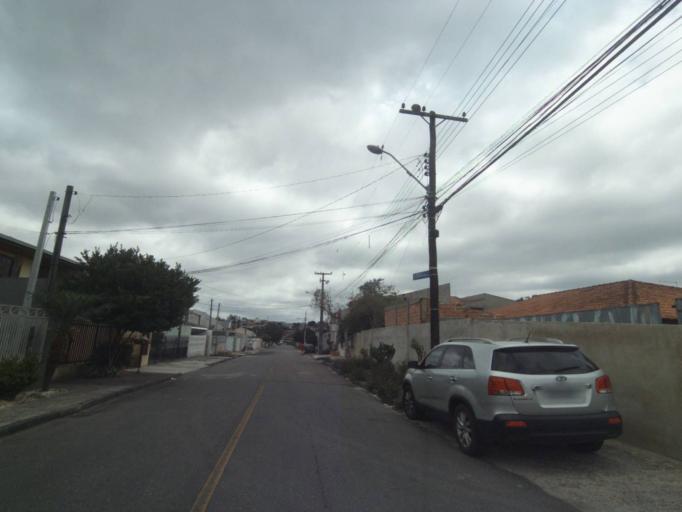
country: BR
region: Parana
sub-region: Sao Jose Dos Pinhais
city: Sao Jose dos Pinhais
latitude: -25.5385
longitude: -49.2528
